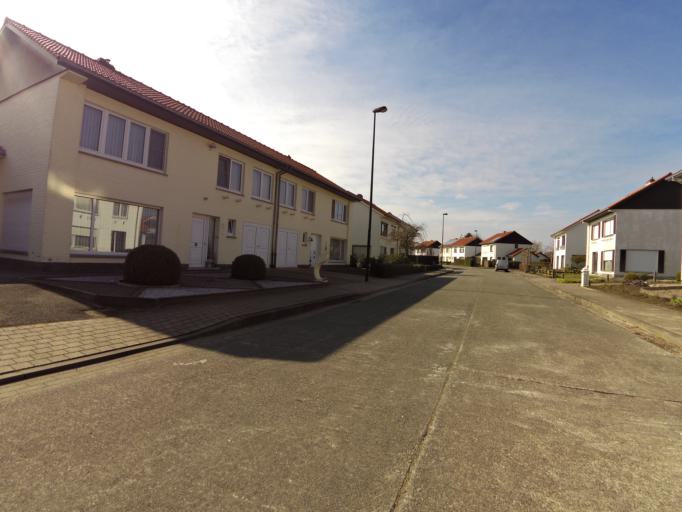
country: BE
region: Flanders
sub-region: Provincie West-Vlaanderen
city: Torhout
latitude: 51.0686
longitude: 3.0831
